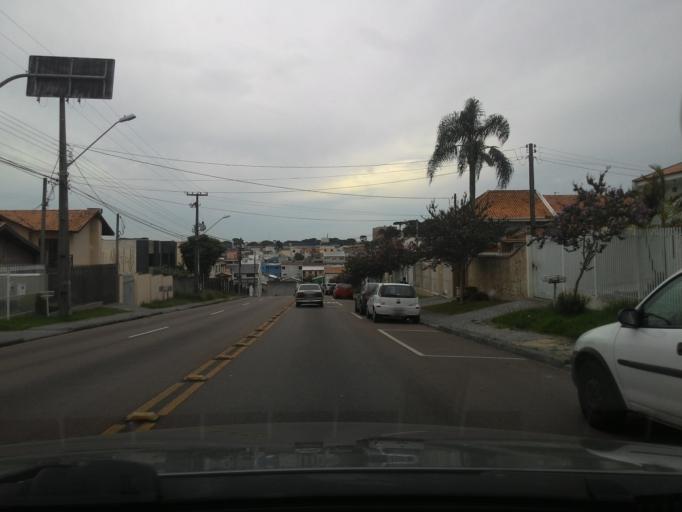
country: BR
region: Parana
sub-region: Pinhais
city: Pinhais
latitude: -25.4458
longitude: -49.2238
